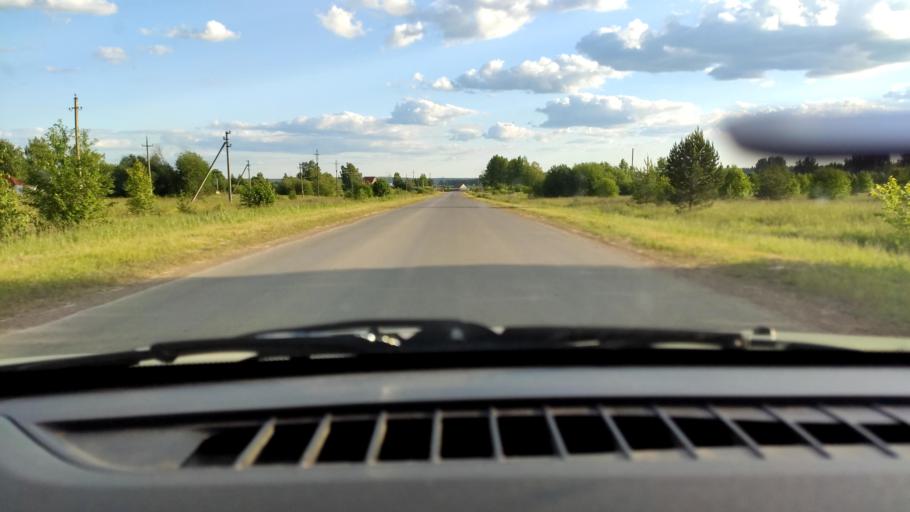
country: RU
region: Perm
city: Uinskoye
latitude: 57.0974
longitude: 56.6440
